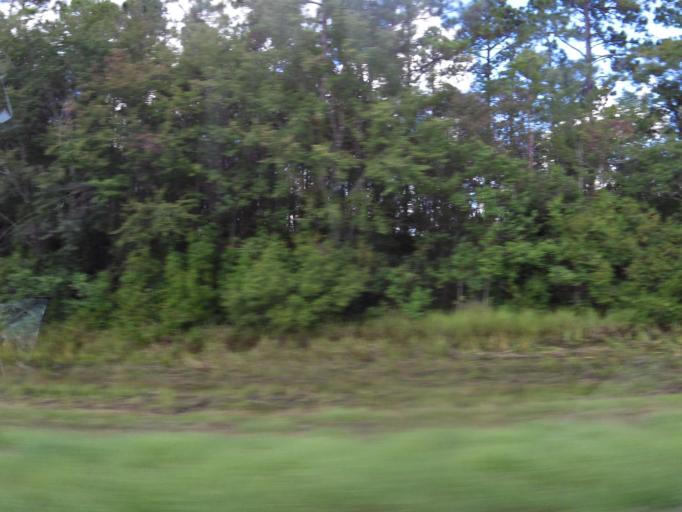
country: US
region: Florida
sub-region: Hamilton County
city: Jasper
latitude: 30.6719
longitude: -82.7630
